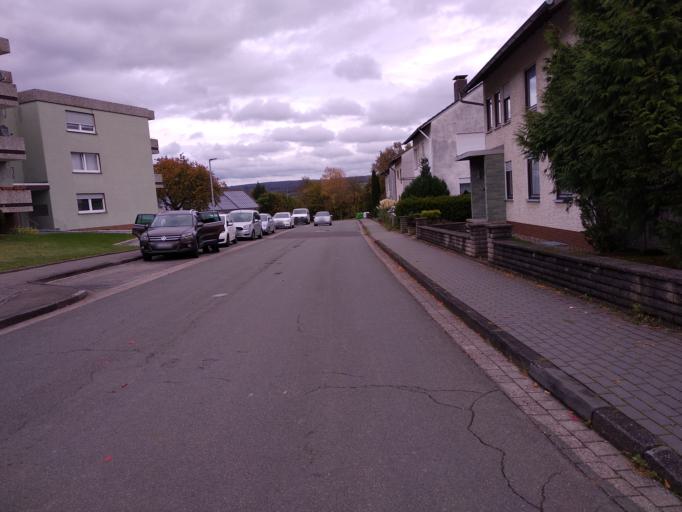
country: DE
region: North Rhine-Westphalia
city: Beverungen
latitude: 51.6630
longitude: 9.3634
